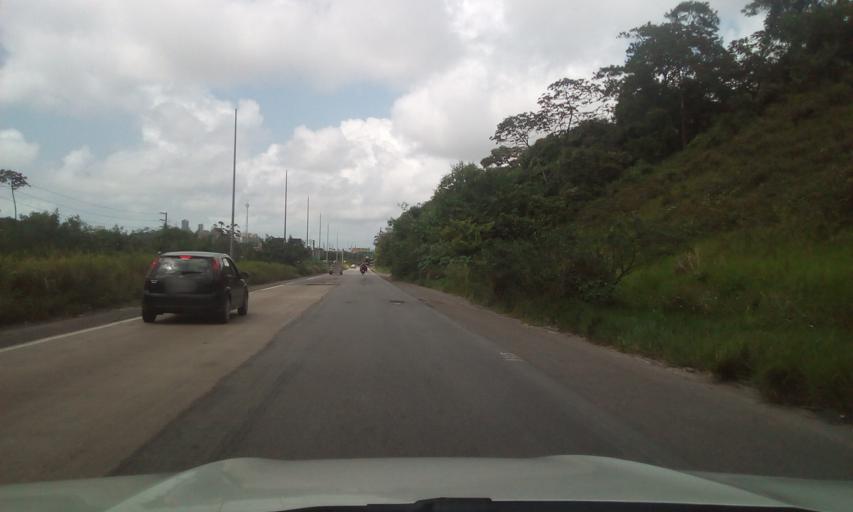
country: BR
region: Pernambuco
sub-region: Recife
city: Recife
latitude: -8.0020
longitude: -34.9386
